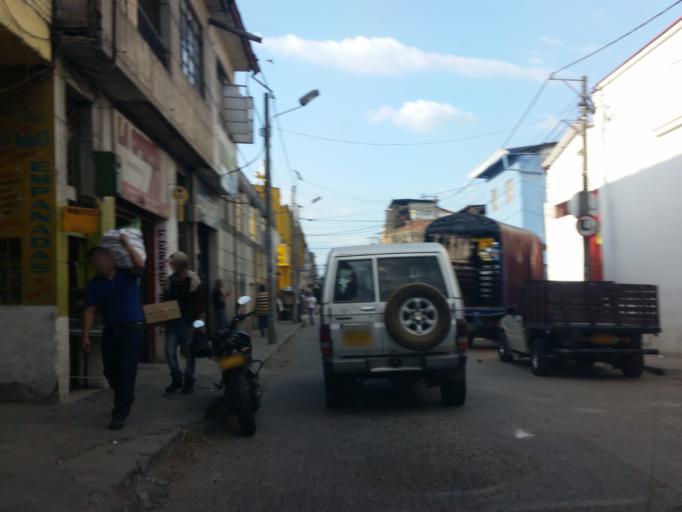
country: CO
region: Caldas
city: Manizales
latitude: 5.0706
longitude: -75.5158
